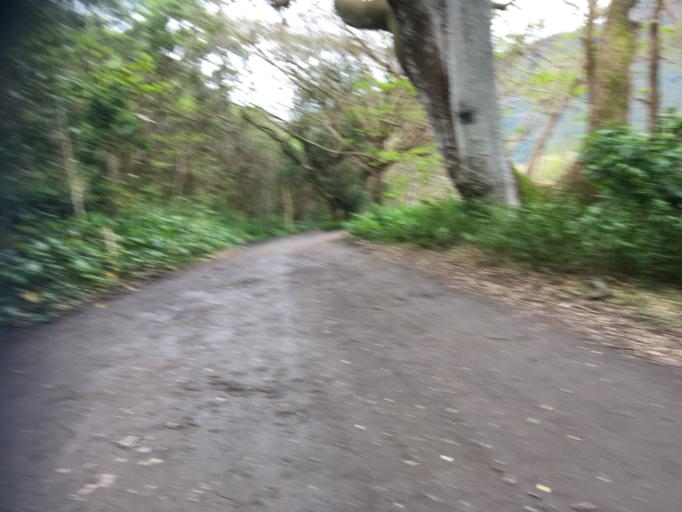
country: US
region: Hawaii
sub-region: Hawaii County
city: Waimea
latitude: 20.1152
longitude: -155.5905
